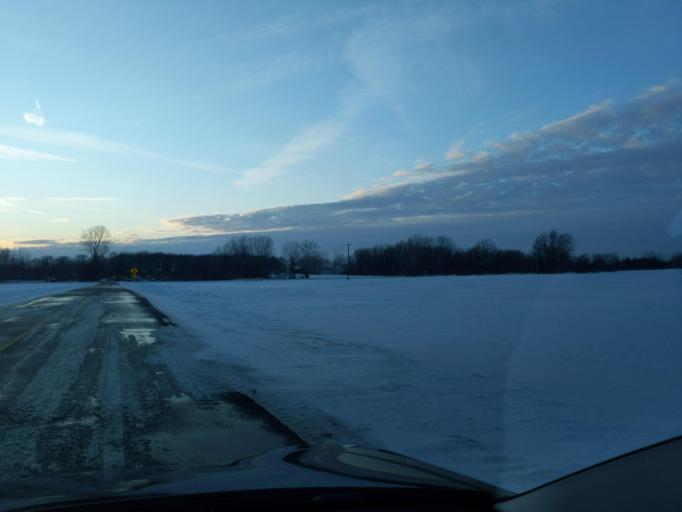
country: US
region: Michigan
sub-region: Ingham County
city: Williamston
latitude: 42.5775
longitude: -84.2953
